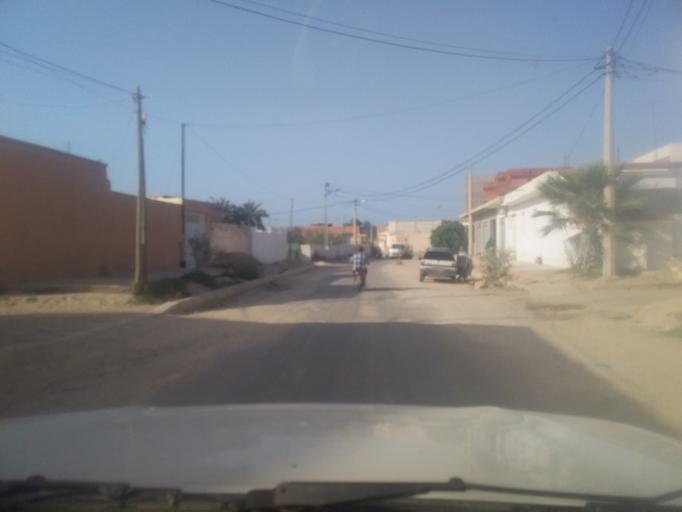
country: TN
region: Qabis
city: Matmata
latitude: 33.6138
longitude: 10.2849
